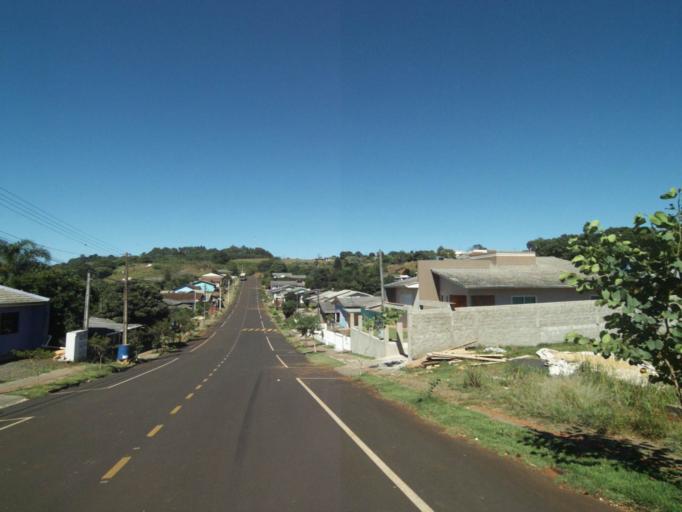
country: BR
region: Santa Catarina
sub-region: Sao Lourenco Do Oeste
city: Sao Lourenco dOeste
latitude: -26.2697
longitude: -52.7819
